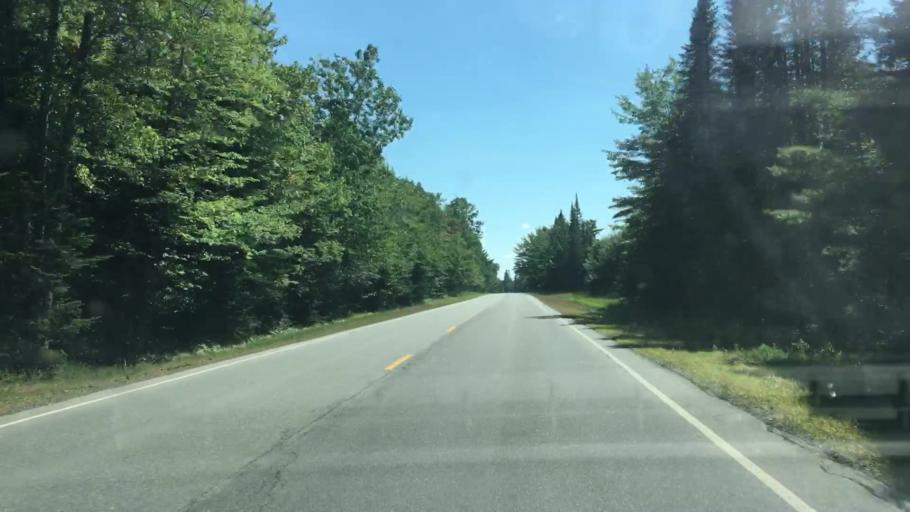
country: US
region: Maine
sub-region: Piscataquis County
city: Milo
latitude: 45.2051
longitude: -68.9083
